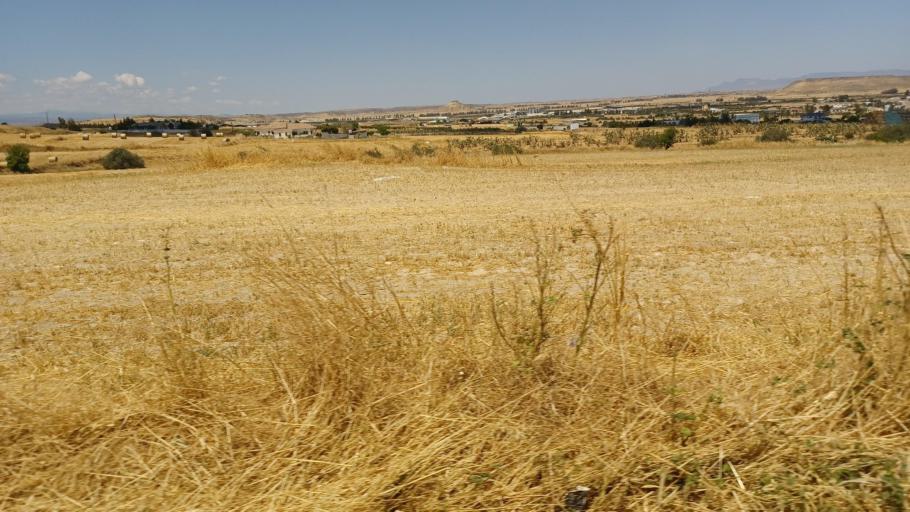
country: CY
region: Larnaka
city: Athienou
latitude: 35.0481
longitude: 33.5414
